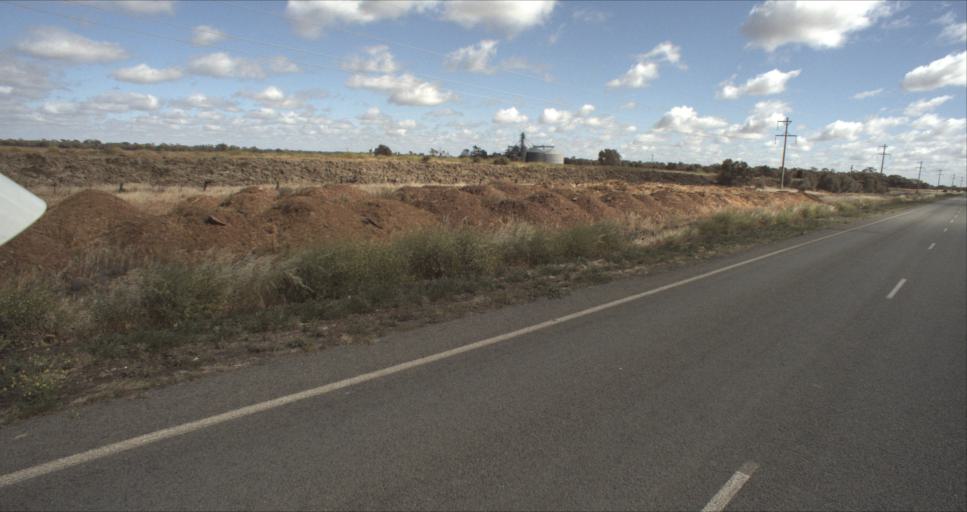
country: AU
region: New South Wales
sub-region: Murrumbidgee Shire
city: Darlington Point
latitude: -34.5512
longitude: 146.1706
